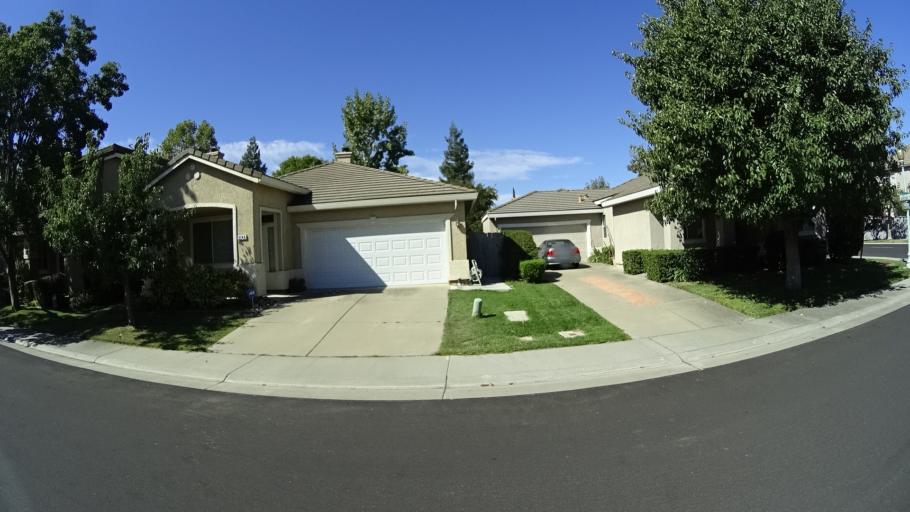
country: US
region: California
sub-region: Sacramento County
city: Laguna
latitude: 38.4169
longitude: -121.4752
